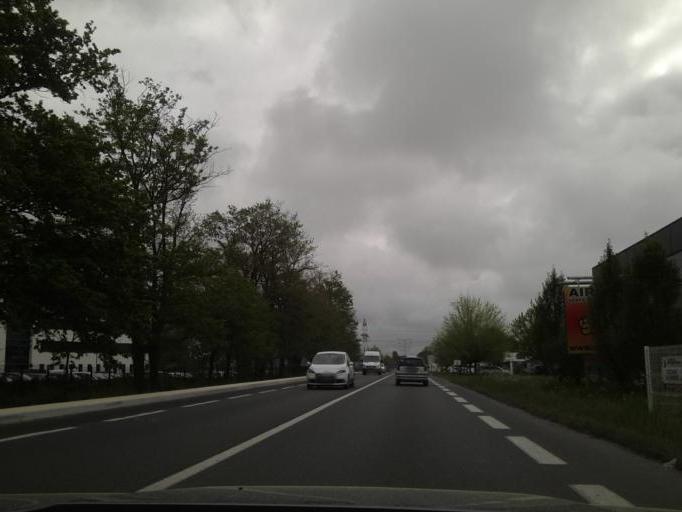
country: FR
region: Aquitaine
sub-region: Departement de la Gironde
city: Le Haillan
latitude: 44.8585
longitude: -0.6712
